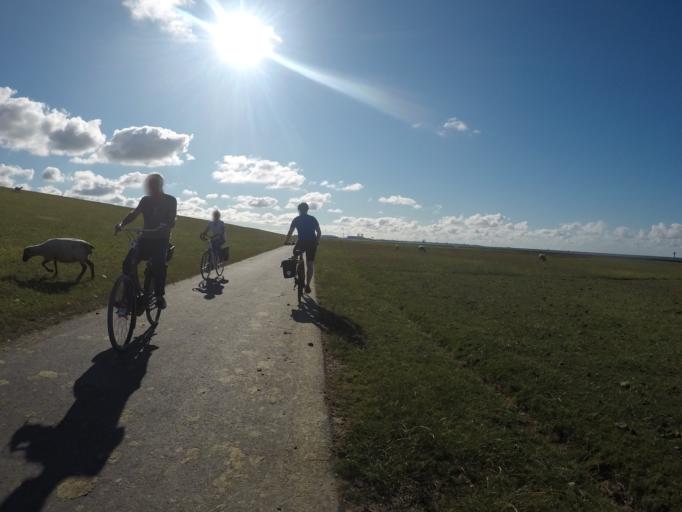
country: DE
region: Lower Saxony
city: Nordleda
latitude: 53.8307
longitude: 8.8181
